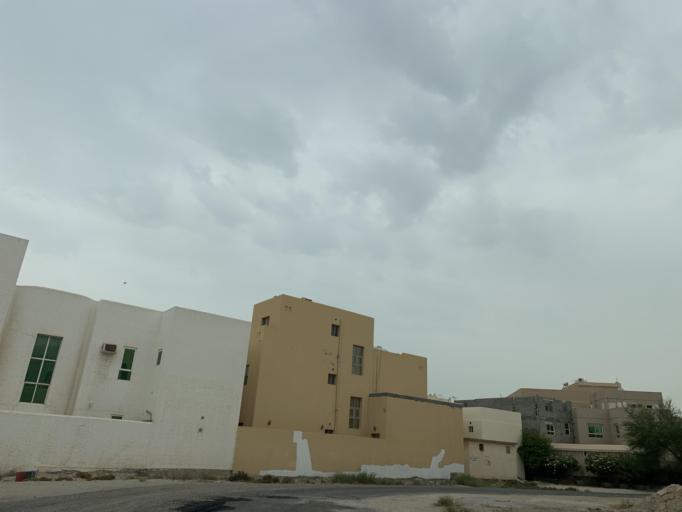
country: BH
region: Northern
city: Madinat `Isa
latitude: 26.1885
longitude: 50.4795
